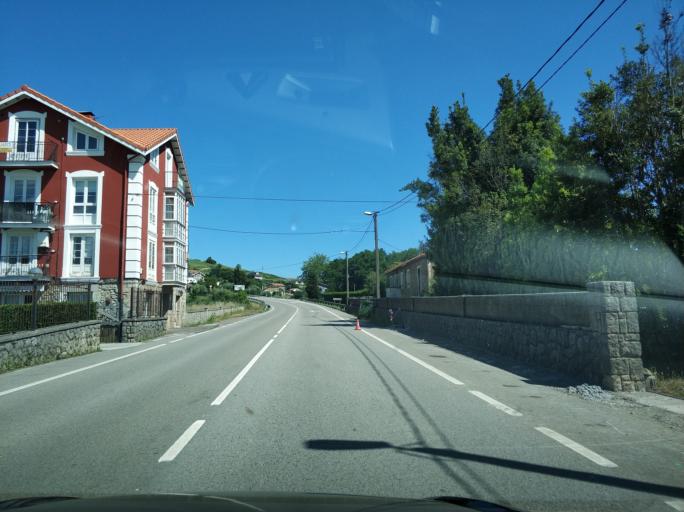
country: ES
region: Cantabria
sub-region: Provincia de Cantabria
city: Camargo
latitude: 43.3882
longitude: -3.8592
